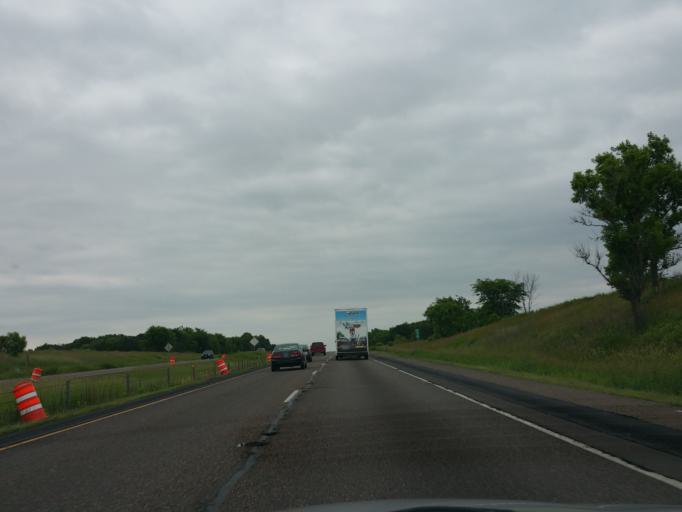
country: US
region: Wisconsin
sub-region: Dunn County
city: Colfax
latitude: 44.8588
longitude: -91.6656
